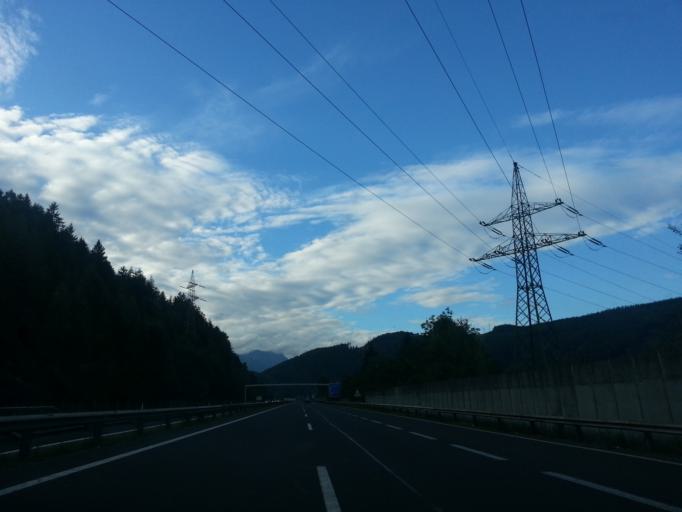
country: AT
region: Styria
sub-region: Politischer Bezirk Leoben
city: Traboch
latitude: 47.3574
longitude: 15.0010
